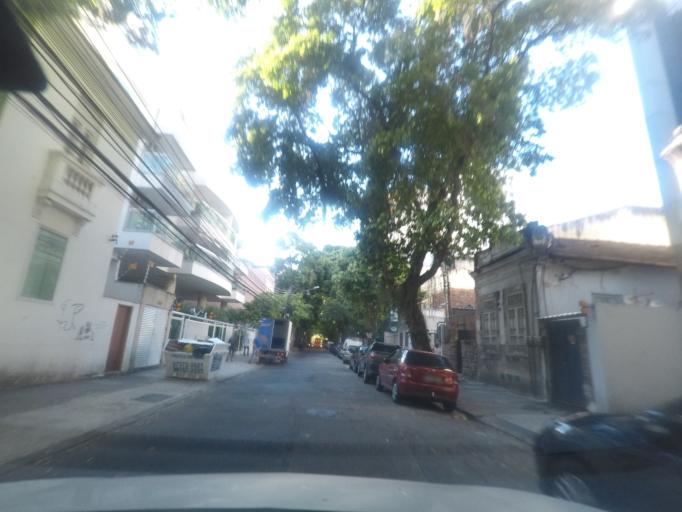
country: BR
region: Rio de Janeiro
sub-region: Rio De Janeiro
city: Rio de Janeiro
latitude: -22.9506
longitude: -43.1874
